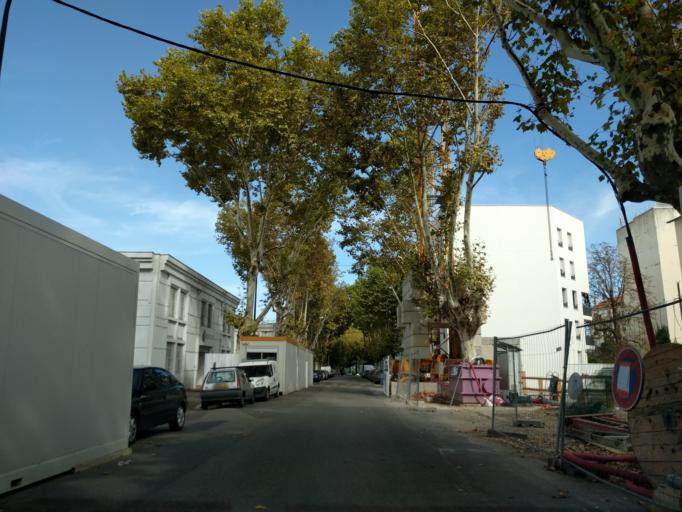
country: FR
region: Rhone-Alpes
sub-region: Departement du Rhone
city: Villeurbanne
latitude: 45.7618
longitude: 4.8768
